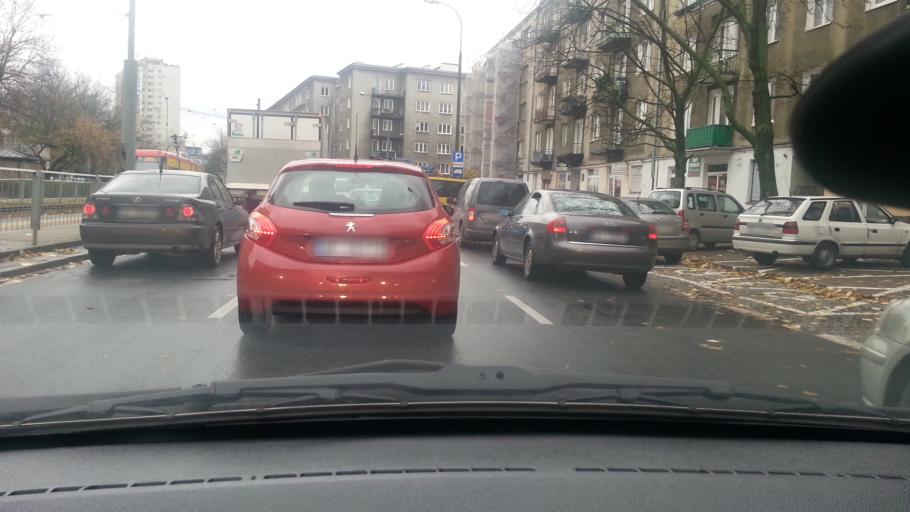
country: PL
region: Masovian Voivodeship
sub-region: Warszawa
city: Wola
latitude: 52.2405
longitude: 20.9775
